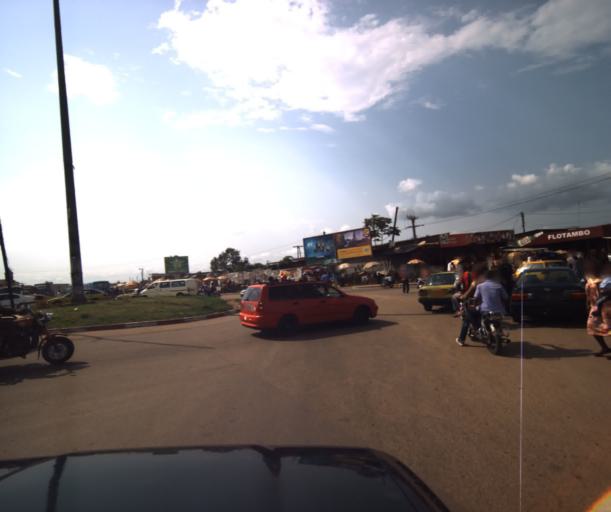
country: CM
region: Littoral
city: Douala
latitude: 4.0117
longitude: 9.7327
